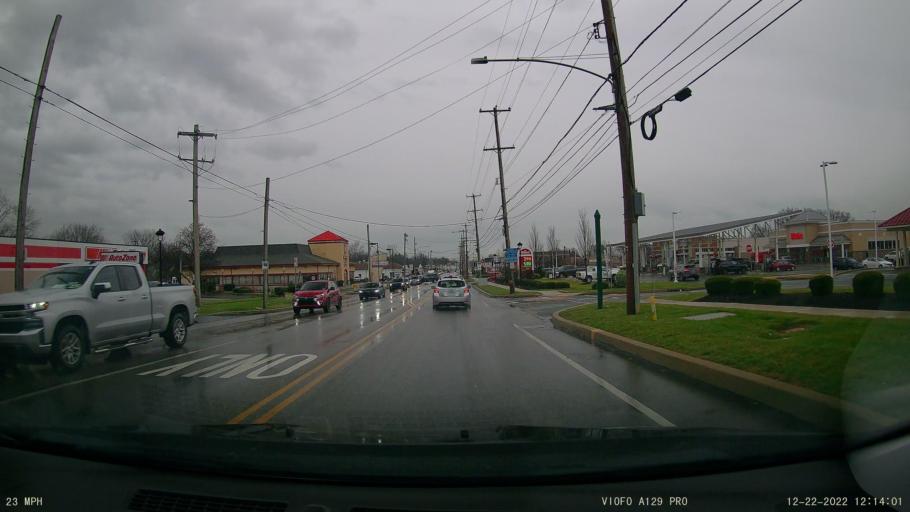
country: US
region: Pennsylvania
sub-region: Montgomery County
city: Trooper
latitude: 40.1420
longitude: -75.3895
